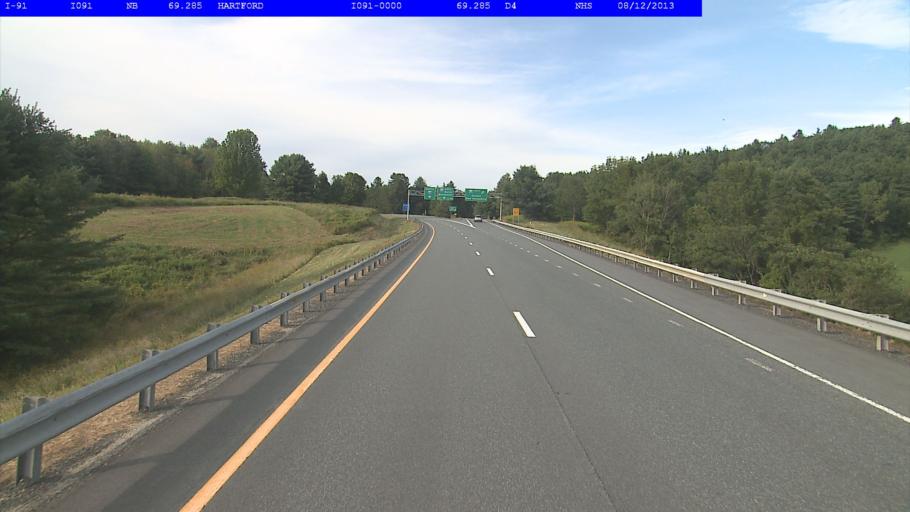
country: US
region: Vermont
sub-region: Windsor County
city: White River Junction
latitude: 43.6322
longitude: -72.3398
